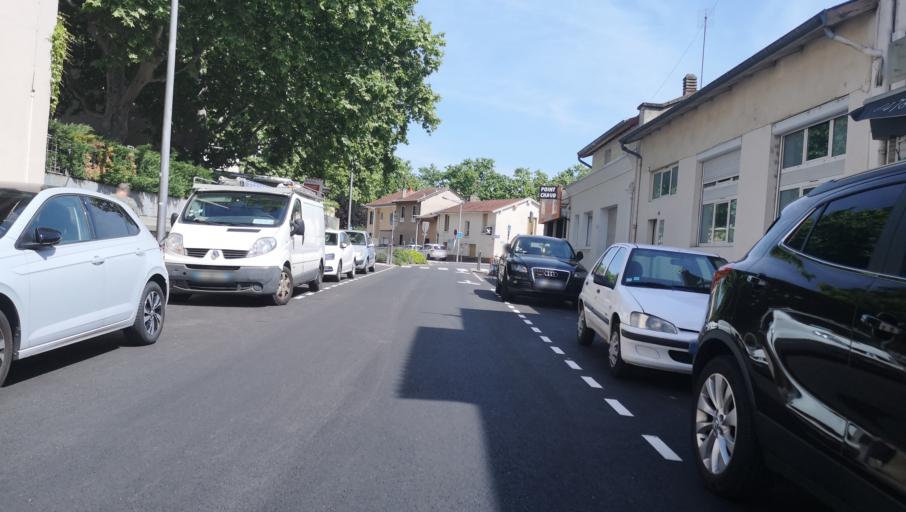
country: FR
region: Rhone-Alpes
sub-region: Departement du Rhone
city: Villeurbanne
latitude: 45.7360
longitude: 4.8812
